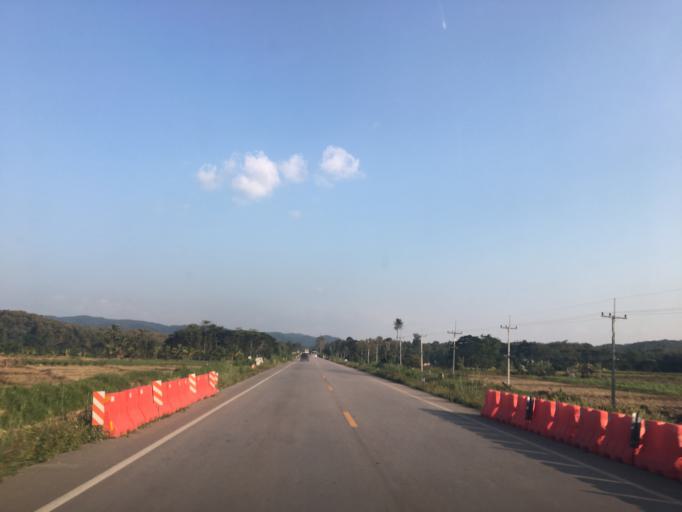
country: TH
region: Lampang
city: Ngao
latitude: 18.7178
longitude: 99.9771
